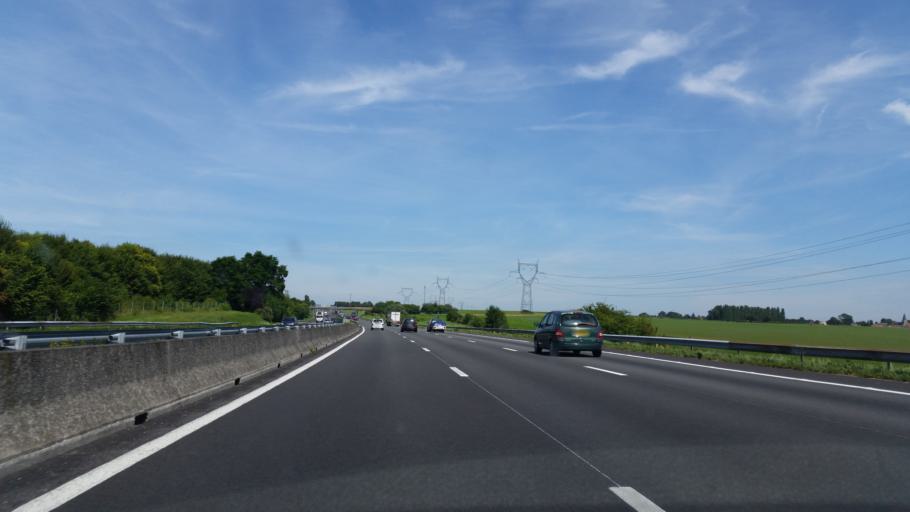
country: FR
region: Picardie
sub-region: Departement de la Somme
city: Peronne
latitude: 49.9051
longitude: 2.8495
